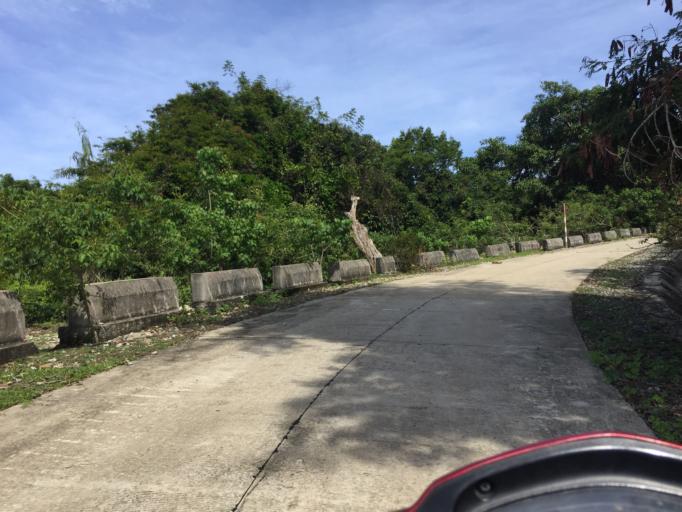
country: VN
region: Quang Nam
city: Hoi An
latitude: 15.9387
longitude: 108.5333
